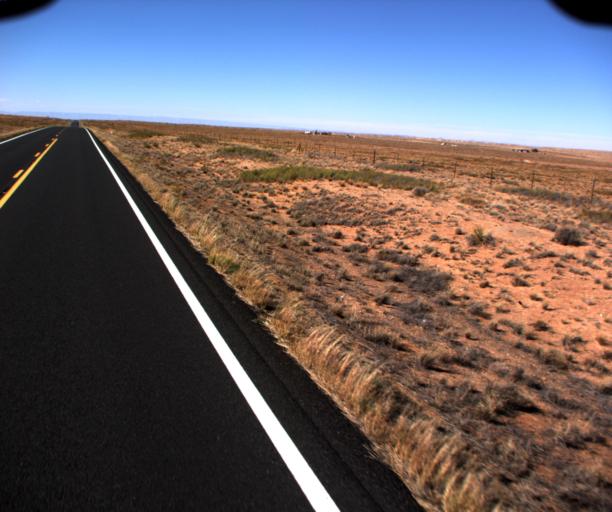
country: US
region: Arizona
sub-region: Coconino County
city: Tuba City
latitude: 36.0173
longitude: -111.1036
